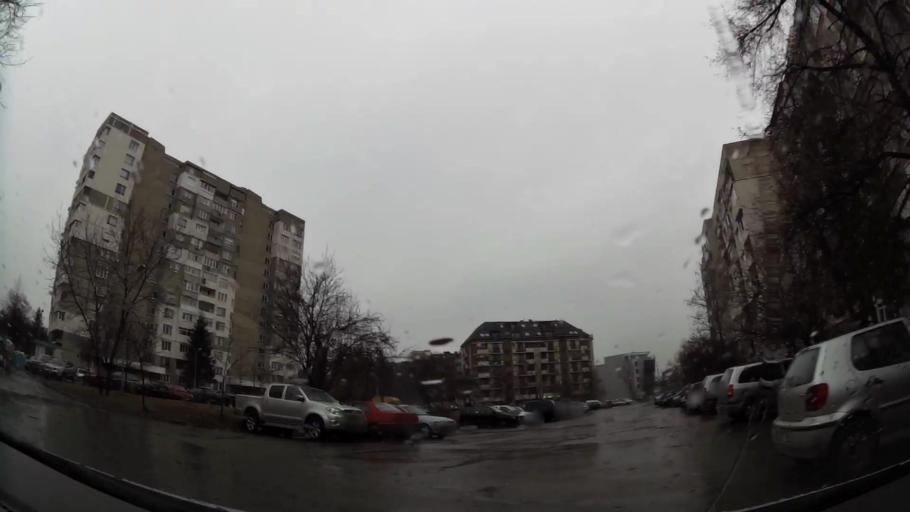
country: BG
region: Sofia-Capital
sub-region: Stolichna Obshtina
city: Sofia
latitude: 42.6506
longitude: 23.3707
